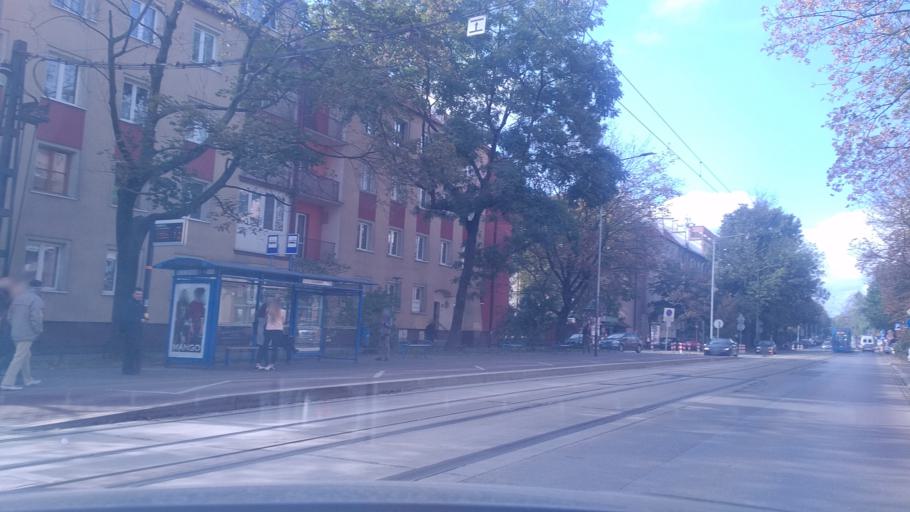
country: PL
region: Lesser Poland Voivodeship
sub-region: Krakow
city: Krakow
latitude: 50.0720
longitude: 19.9196
